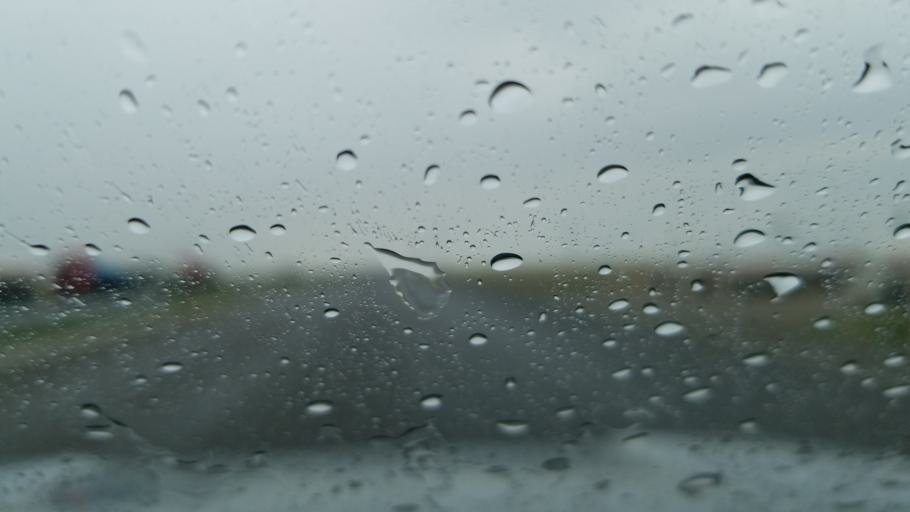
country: TM
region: Balkan
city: Serdar
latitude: 39.0119
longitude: 56.2333
